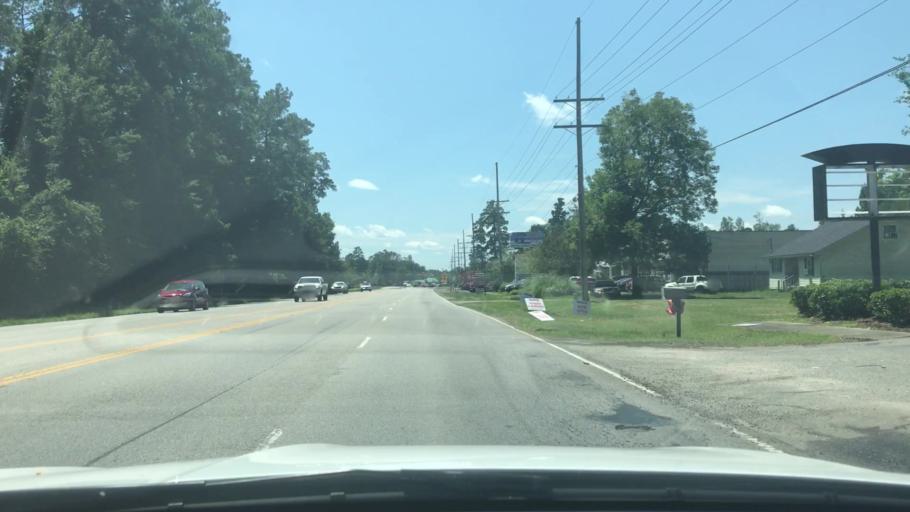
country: US
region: South Carolina
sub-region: Horry County
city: Conway
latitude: 33.8705
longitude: -79.0521
